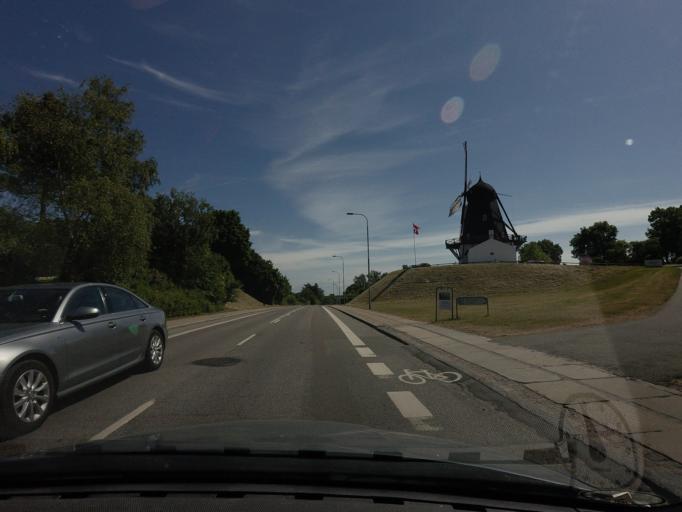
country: DK
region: Central Jutland
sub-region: Norddjurs Kommune
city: Grenaa
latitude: 56.4222
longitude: 10.8637
